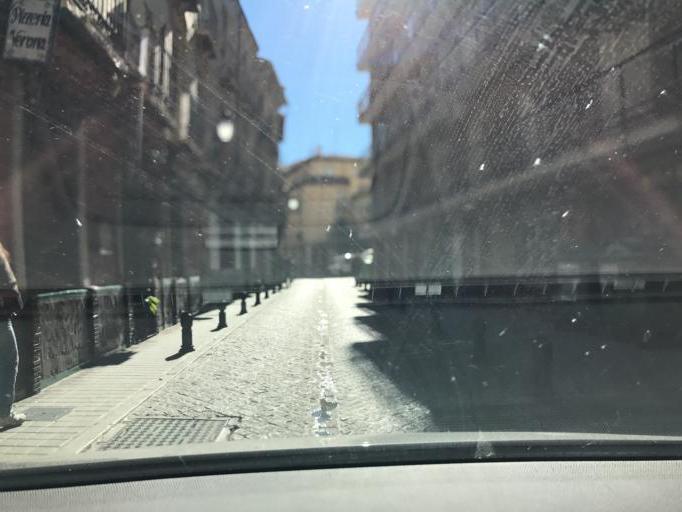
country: ES
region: Andalusia
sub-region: Provincia de Granada
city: Granada
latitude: 37.1809
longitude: -3.5990
